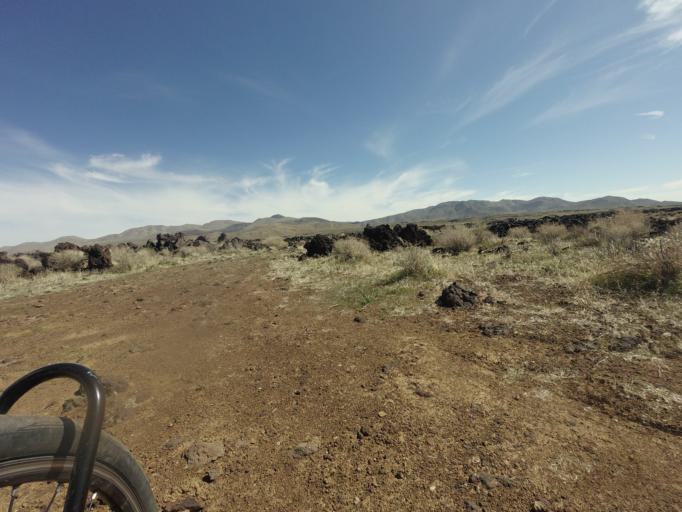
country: US
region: California
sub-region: Kern County
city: Inyokern
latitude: 35.9755
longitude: -117.9103
